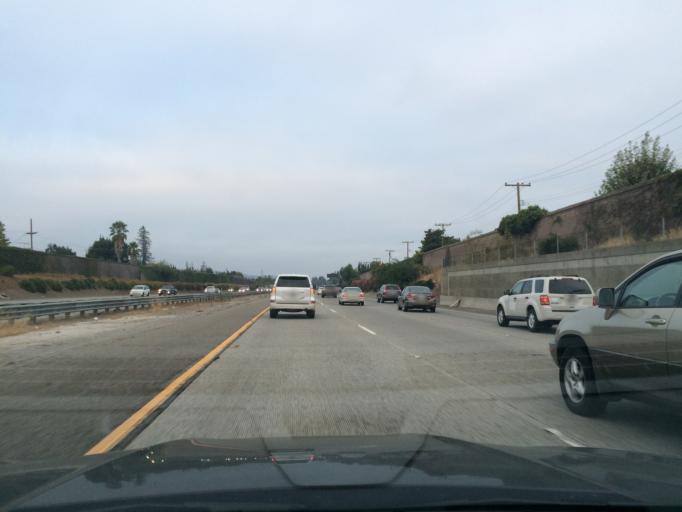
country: US
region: California
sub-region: Santa Clara County
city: Cambrian Park
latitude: 37.2538
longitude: -121.8818
